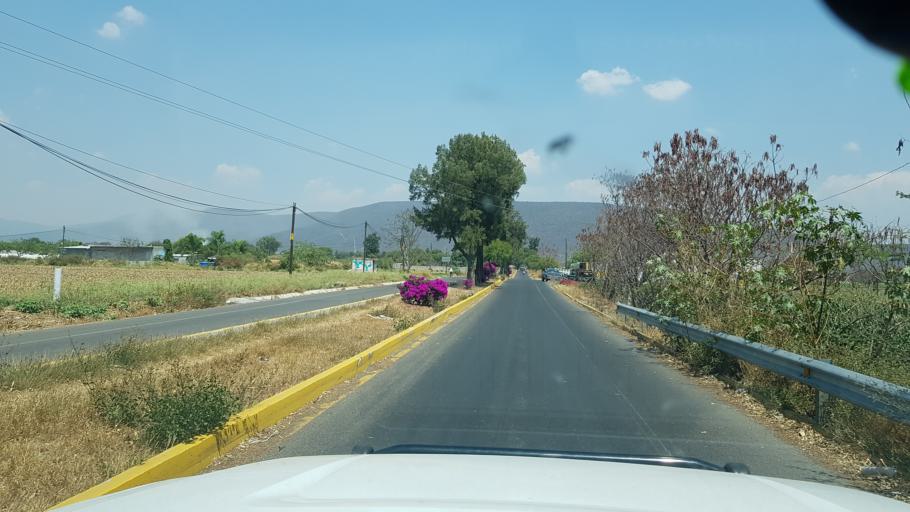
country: MX
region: Puebla
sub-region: Huaquechula
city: Cacaloxuchitl
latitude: 18.7901
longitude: -98.4605
